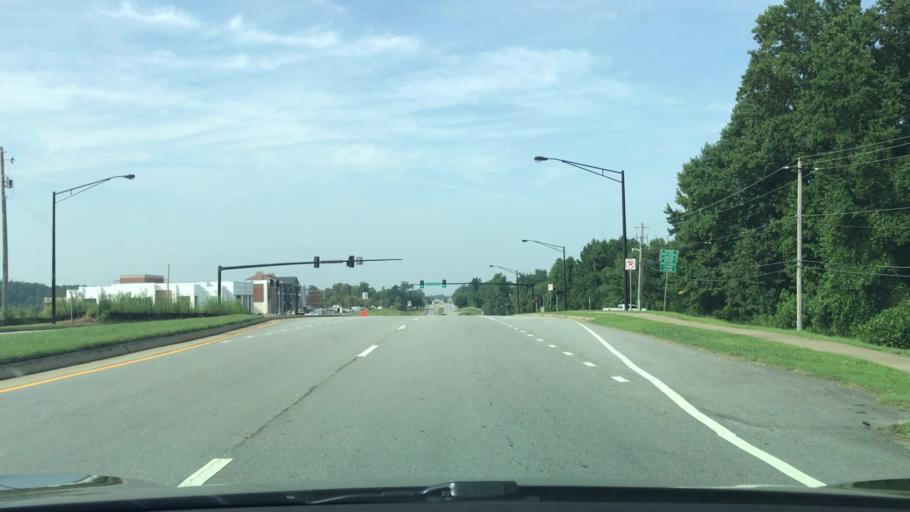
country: US
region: Georgia
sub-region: Gwinnett County
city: Buford
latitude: 34.1221
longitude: -83.9876
